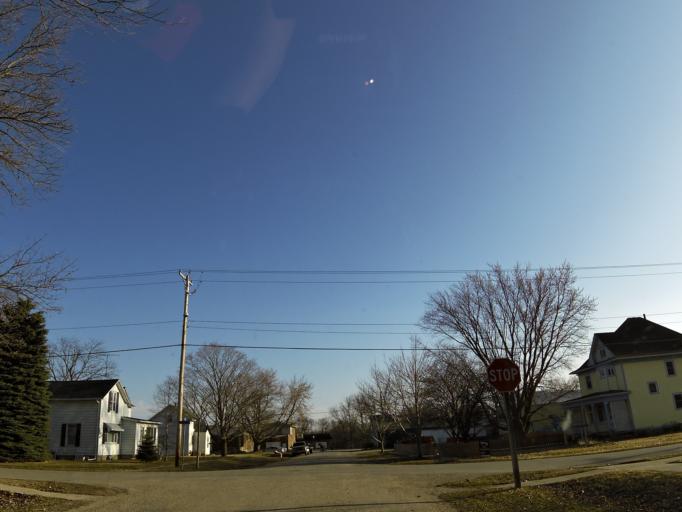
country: US
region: Iowa
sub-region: Worth County
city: Northwood
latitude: 43.4454
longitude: -93.2235
